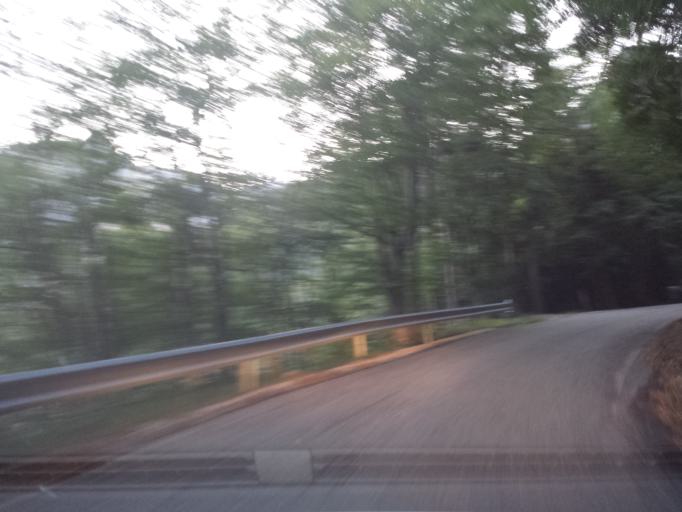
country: IT
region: Veneto
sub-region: Provincia di Vicenza
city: Recoaro Terme
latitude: 45.7221
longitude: 11.1781
